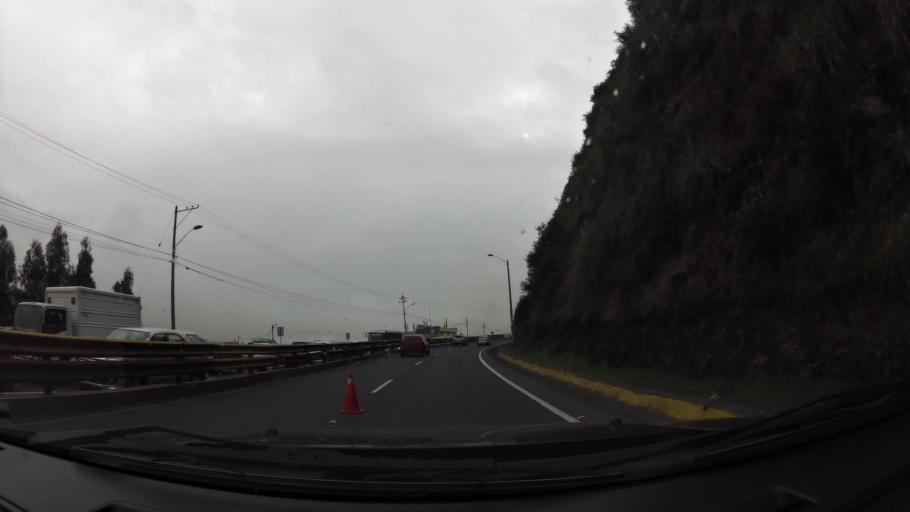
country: EC
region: Pichincha
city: Quito
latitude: -0.2277
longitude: -78.4944
